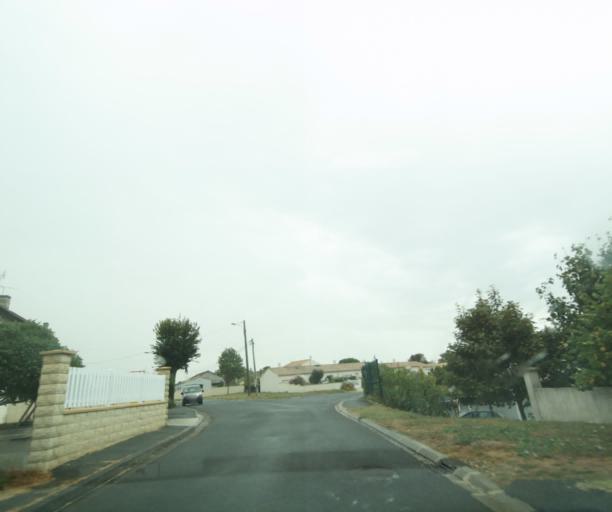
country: FR
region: Poitou-Charentes
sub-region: Departement de la Charente-Maritime
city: Tonnay-Charente
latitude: 45.9450
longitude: -0.9033
